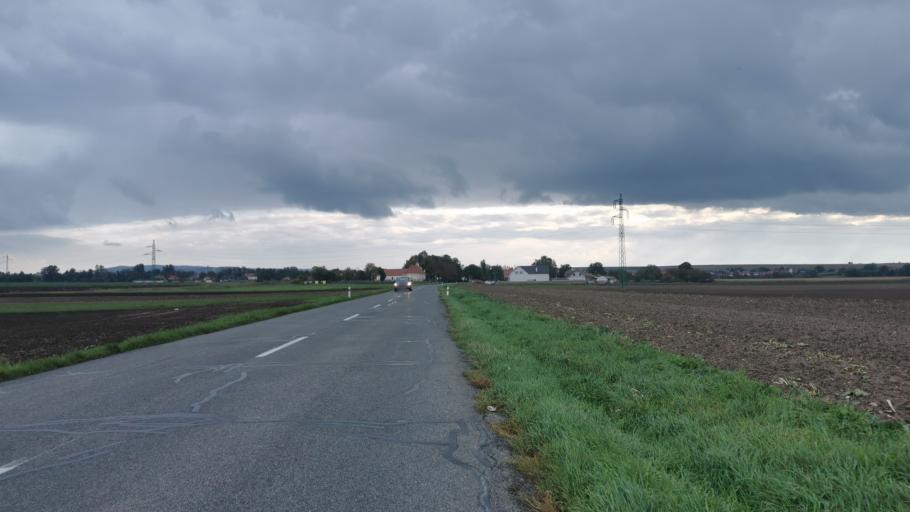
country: SK
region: Trnavsky
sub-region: Okres Skalica
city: Holic
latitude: 48.8128
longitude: 17.1945
